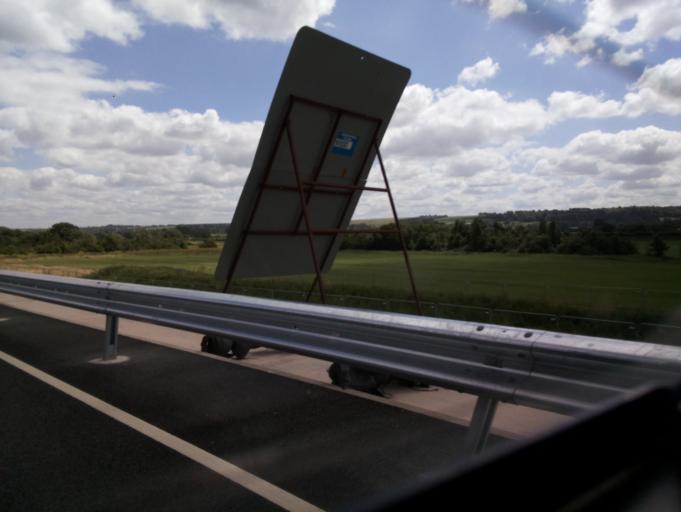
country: GB
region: England
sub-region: Wiltshire
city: Lydiard Tregoze
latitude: 51.5412
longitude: -1.8342
